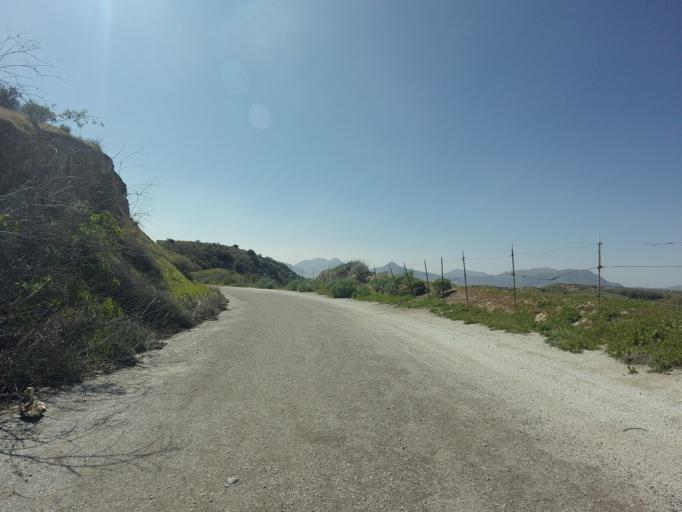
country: US
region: California
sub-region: Riverside County
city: Lakeview
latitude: 33.9033
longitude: -117.0623
